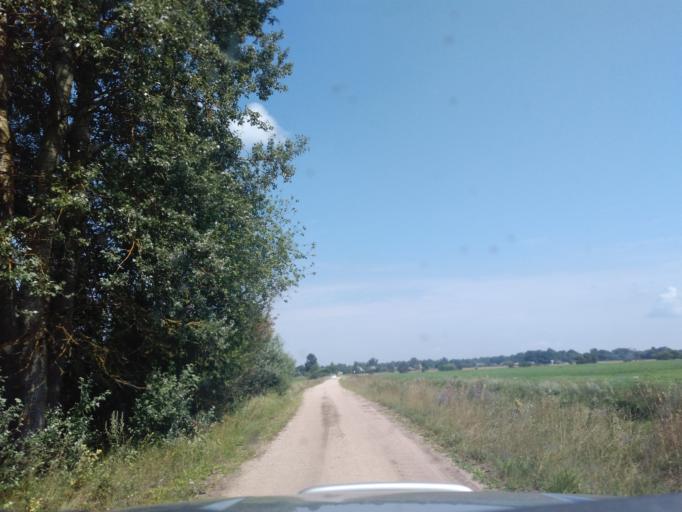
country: BY
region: Minsk
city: Valozhyn
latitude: 54.0035
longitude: 26.5709
